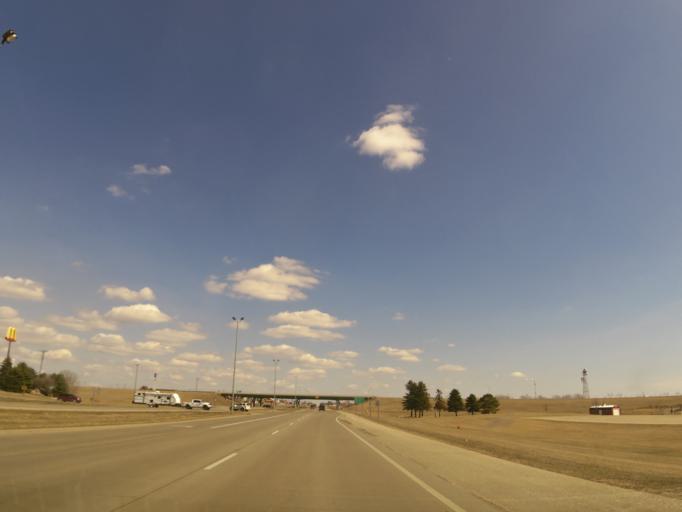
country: US
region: South Dakota
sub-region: Codington County
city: Watertown
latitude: 44.8899
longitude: -97.0611
